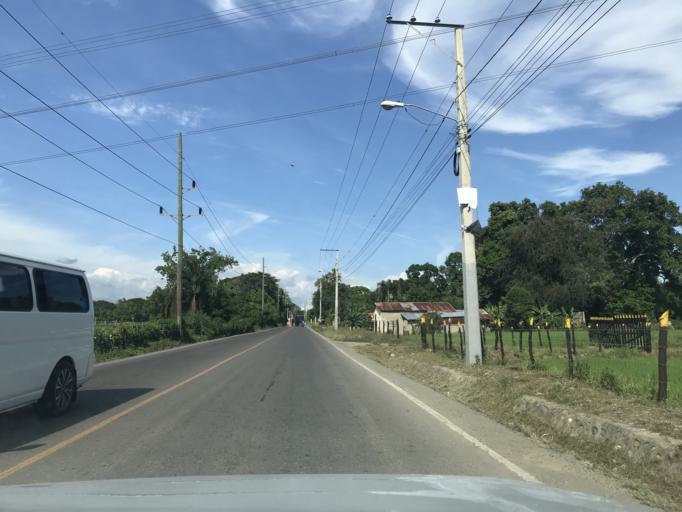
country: DO
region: Santiago
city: Santiago de los Caballeros
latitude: 19.4517
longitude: -70.7535
